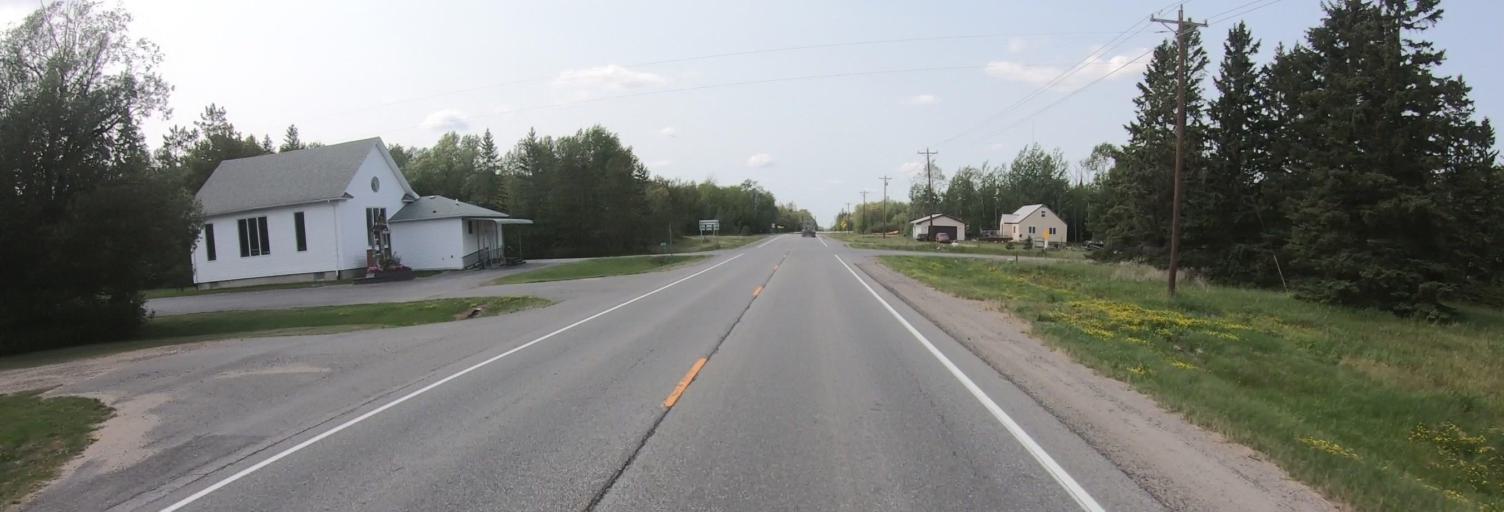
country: US
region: Minnesota
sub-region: Lake of the Woods County
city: Baudette
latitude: 48.6270
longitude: -94.1009
